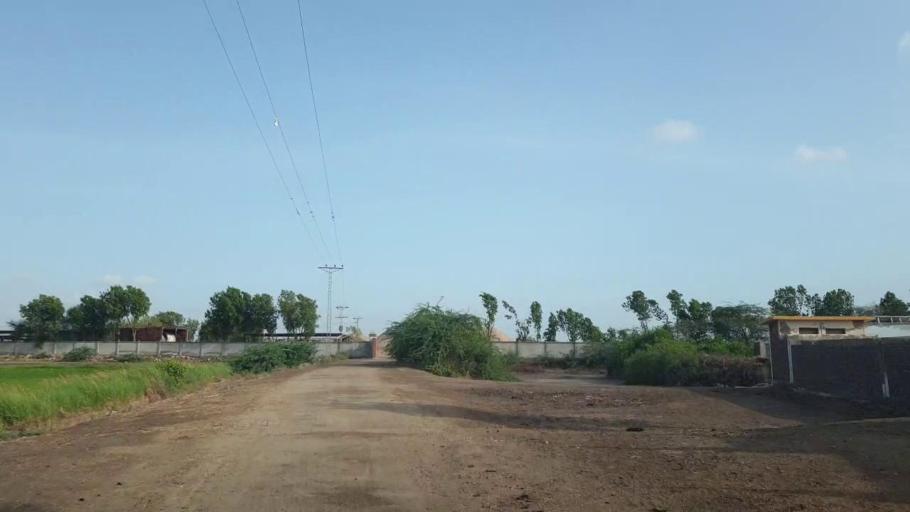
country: PK
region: Sindh
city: Kadhan
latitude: 24.6230
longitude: 69.0857
